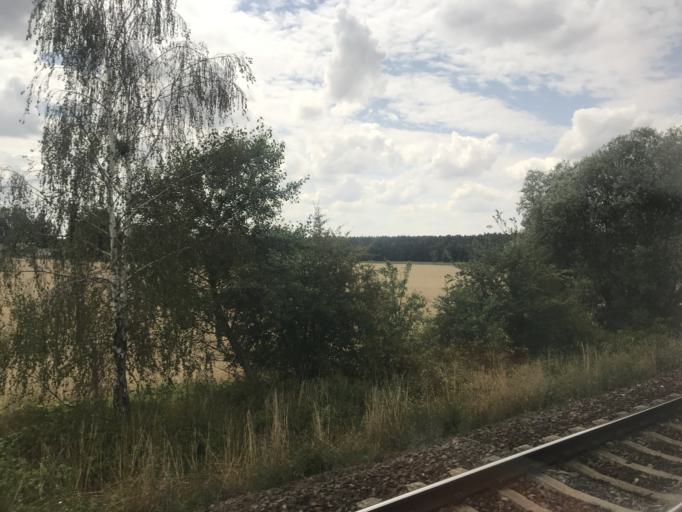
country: PL
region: Greater Poland Voivodeship
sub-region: Powiat poznanski
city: Dopiewo
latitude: 52.3465
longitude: 16.6324
